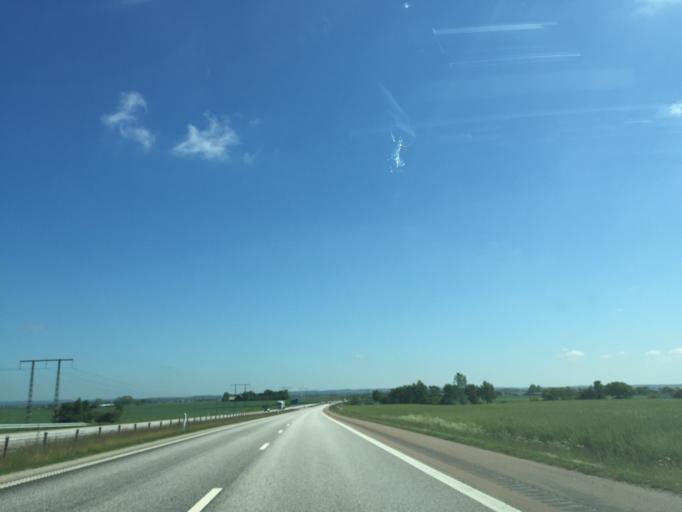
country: SE
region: Skane
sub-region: Astorps Kommun
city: Astorp
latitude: 56.1519
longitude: 12.9455
